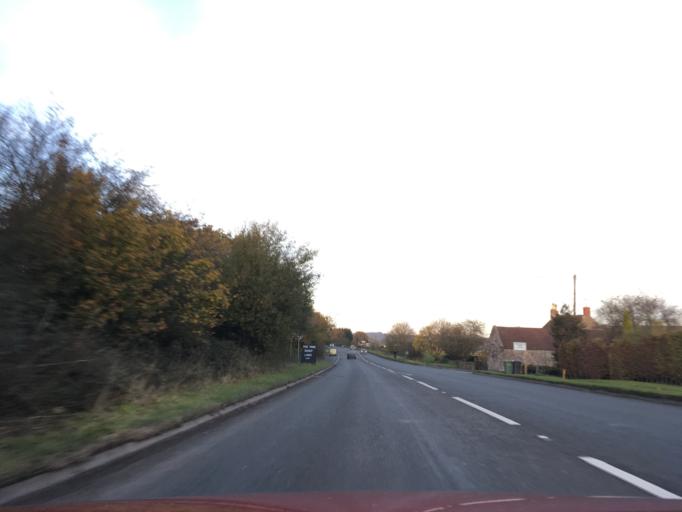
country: GB
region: England
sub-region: South Gloucestershire
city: Falfield
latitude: 51.6244
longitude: -2.4671
